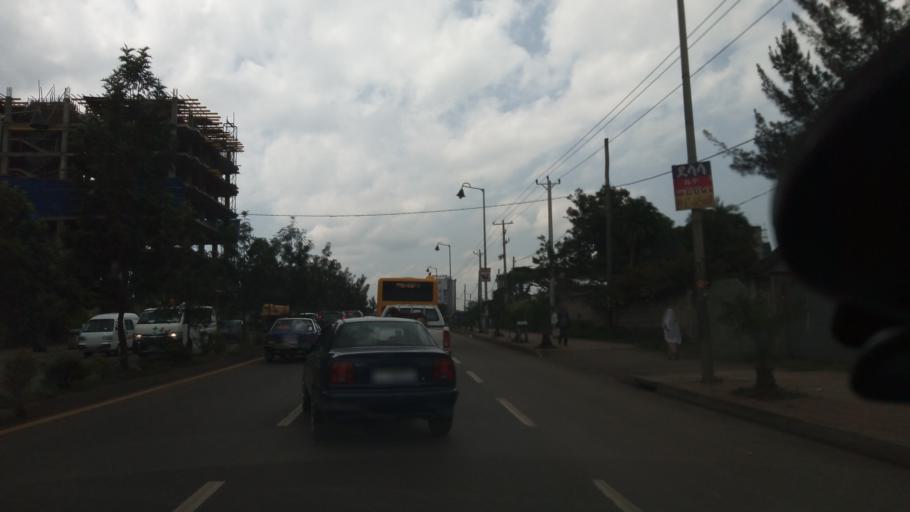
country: ET
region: Adis Abeba
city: Addis Ababa
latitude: 8.9910
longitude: 38.7196
